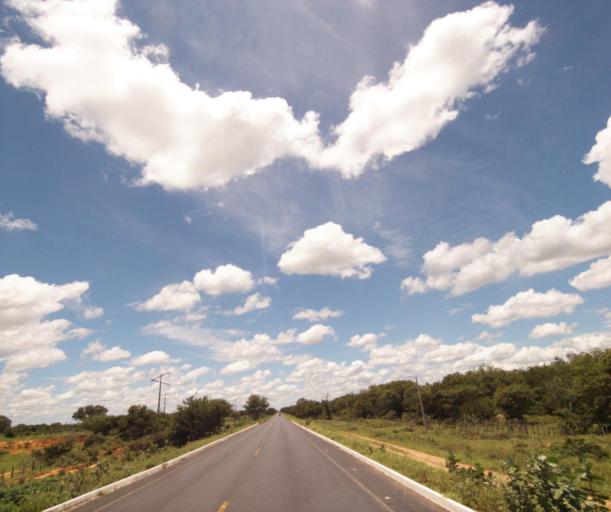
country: BR
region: Bahia
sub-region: Bom Jesus Da Lapa
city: Bom Jesus da Lapa
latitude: -13.2584
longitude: -43.4772
